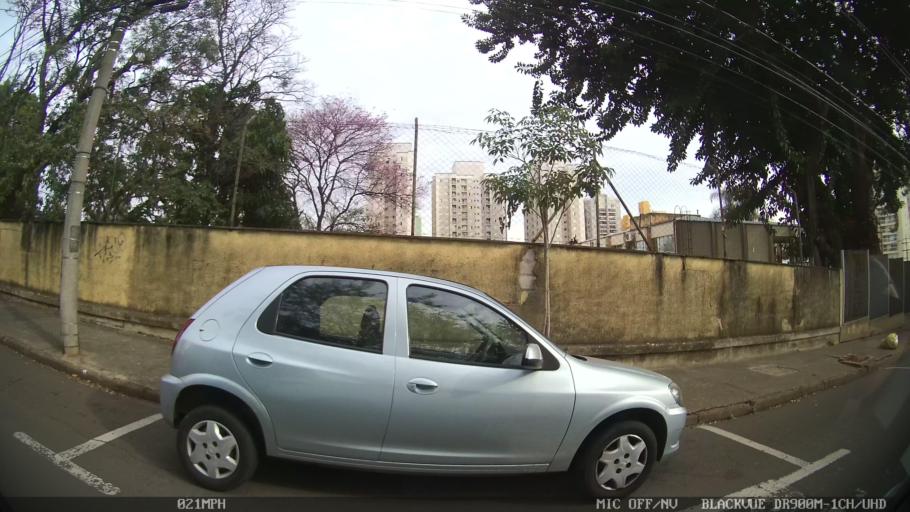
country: BR
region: Sao Paulo
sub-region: Piracicaba
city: Piracicaba
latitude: -22.7245
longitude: -47.6352
